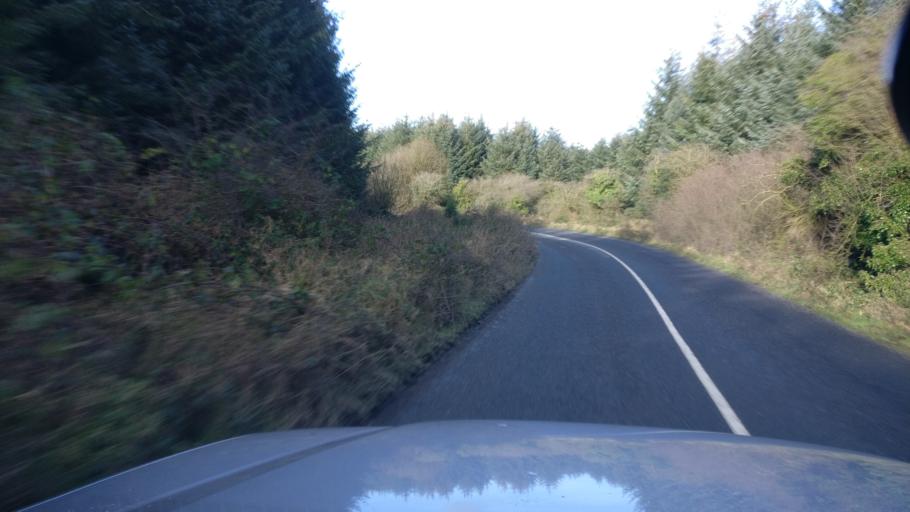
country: IE
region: Leinster
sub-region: Laois
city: Stradbally
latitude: 52.9123
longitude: -7.1830
